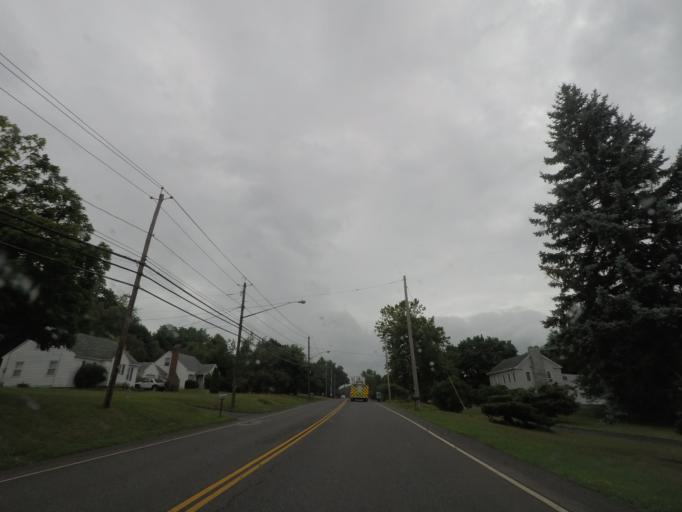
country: US
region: New York
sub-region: Albany County
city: West Albany
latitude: 42.6792
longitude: -73.7574
